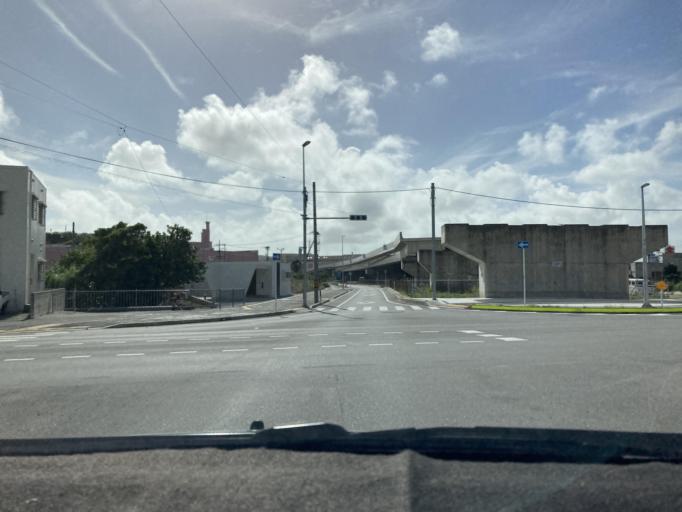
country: JP
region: Okinawa
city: Naha-shi
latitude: 26.2044
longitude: 127.7342
